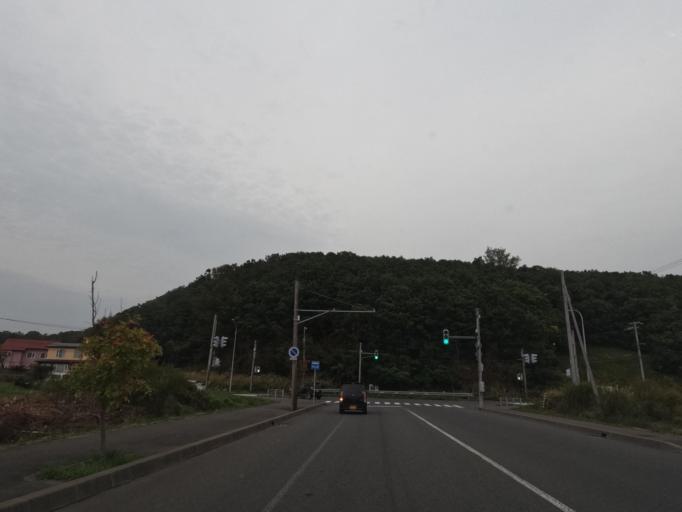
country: JP
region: Hokkaido
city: Date
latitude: 42.3833
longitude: 140.9118
